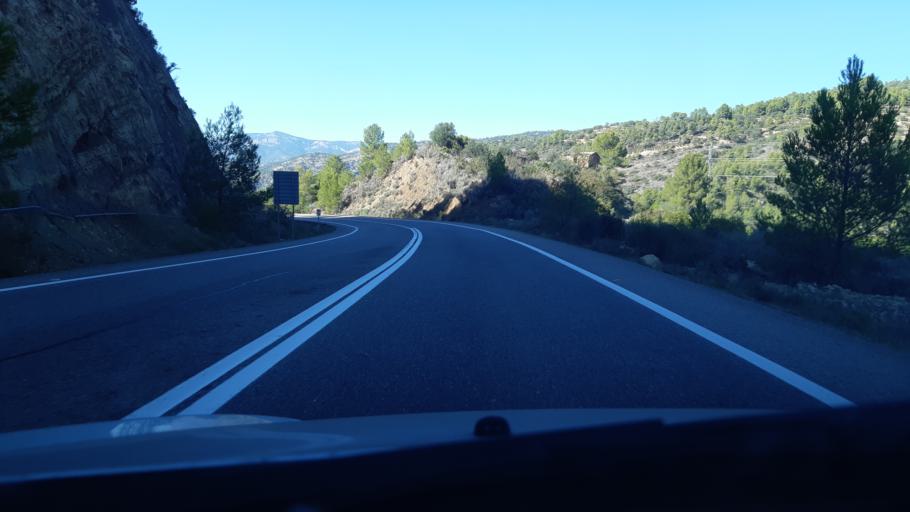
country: ES
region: Catalonia
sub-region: Provincia de Tarragona
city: Rasquera
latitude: 40.9952
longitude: 0.5678
